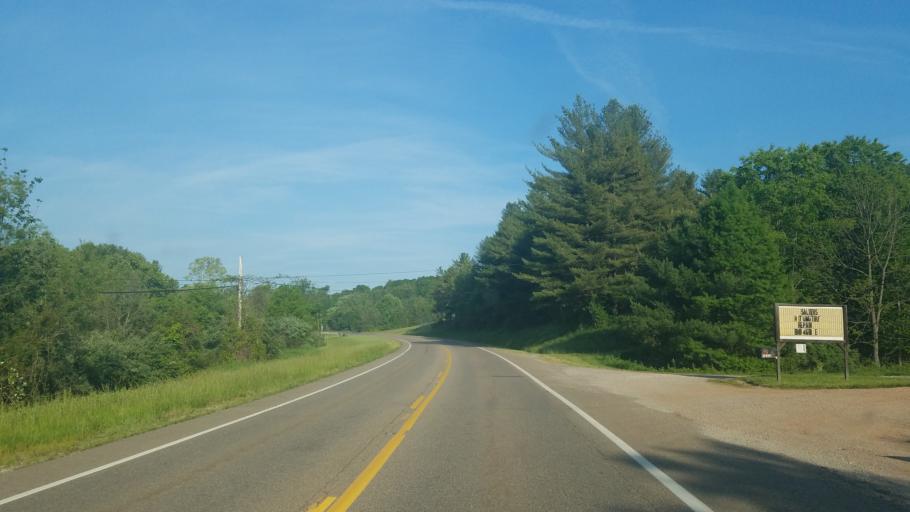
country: US
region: West Virginia
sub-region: Mason County
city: New Haven
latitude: 39.1173
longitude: -81.9059
